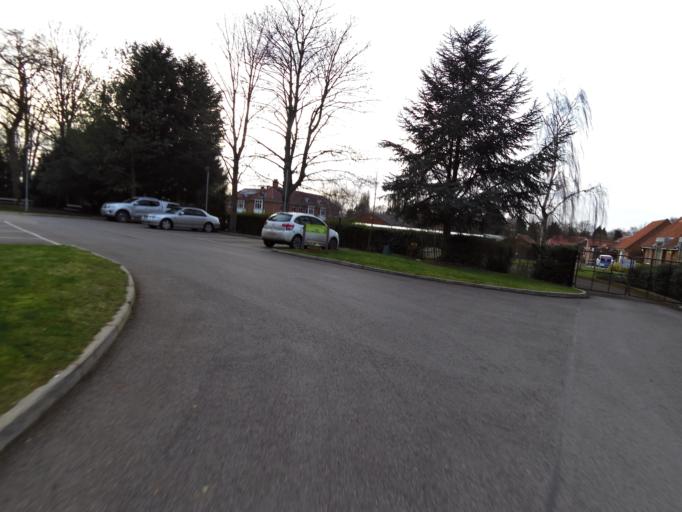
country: GB
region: England
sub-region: City of York
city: York
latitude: 53.9690
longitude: -1.1027
